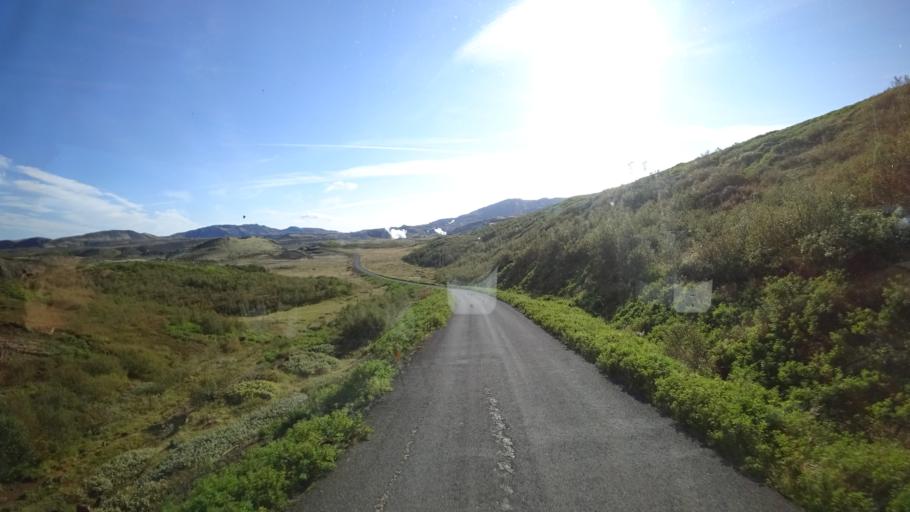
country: IS
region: South
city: Hveragerdi
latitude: 64.1316
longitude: -21.2508
